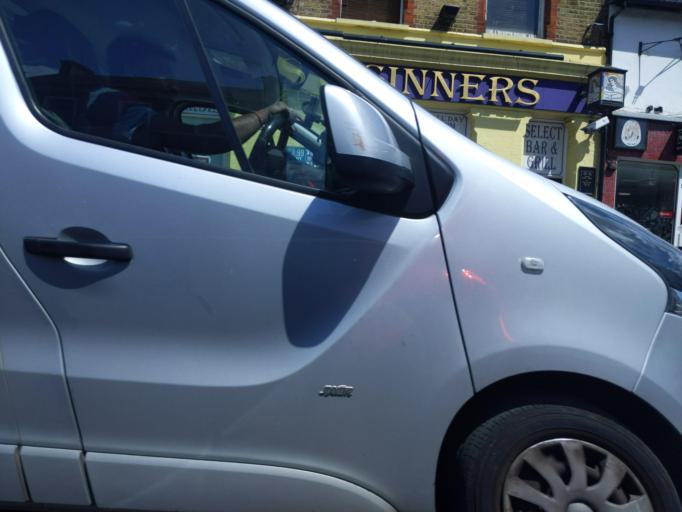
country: GB
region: England
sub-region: Greater London
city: Croydon
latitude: 51.3877
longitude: -0.1110
